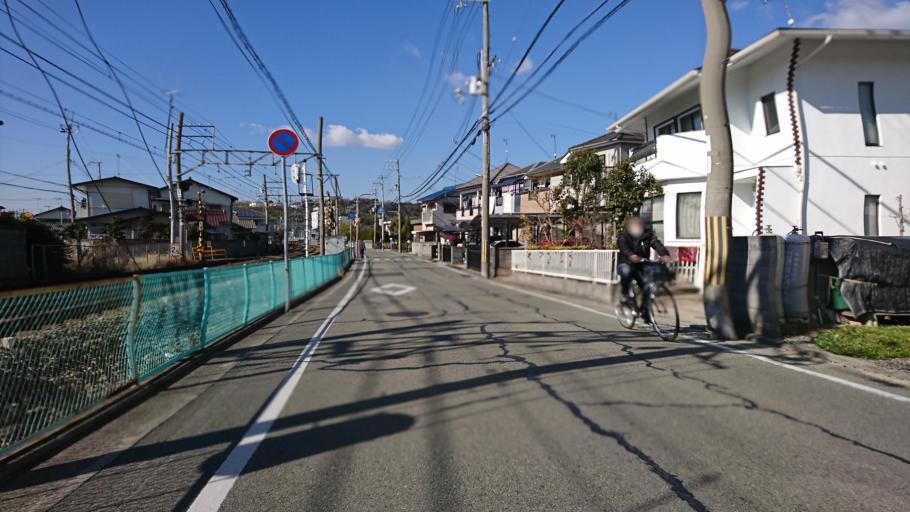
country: JP
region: Hyogo
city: Kakogawacho-honmachi
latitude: 34.7747
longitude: 134.7759
